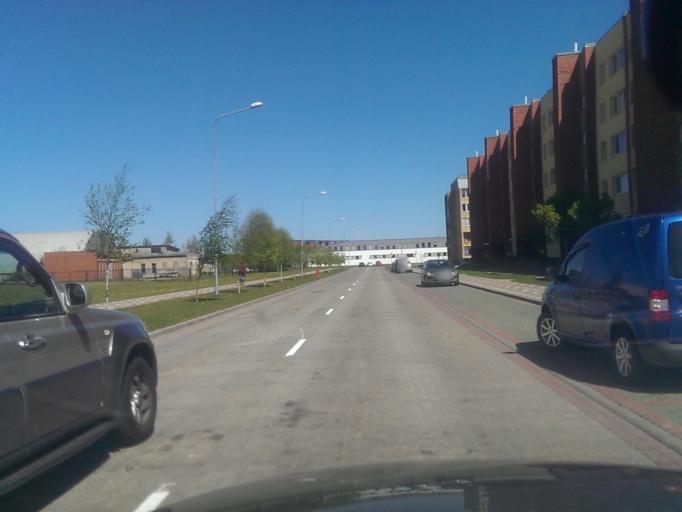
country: LV
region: Ventspils
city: Ventspils
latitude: 57.4030
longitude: 21.6082
